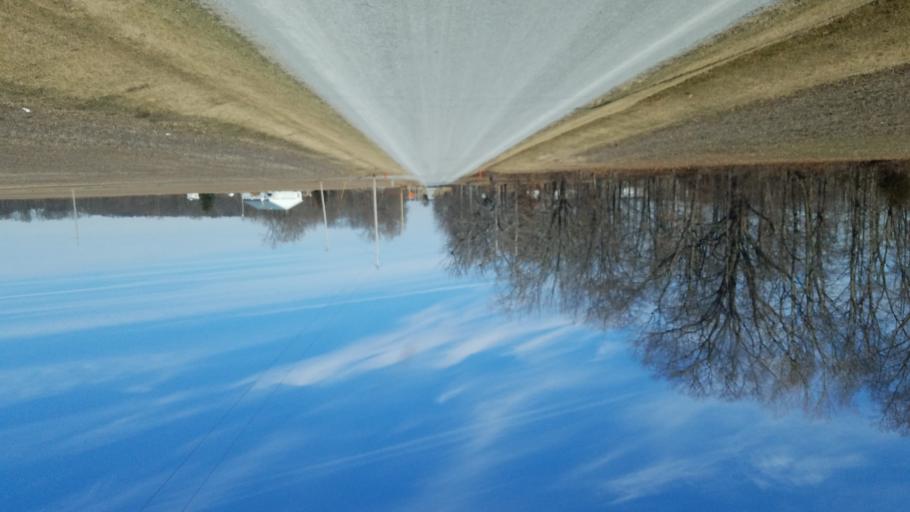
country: US
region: Ohio
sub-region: Hardin County
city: Kenton
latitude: 40.5975
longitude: -83.4813
